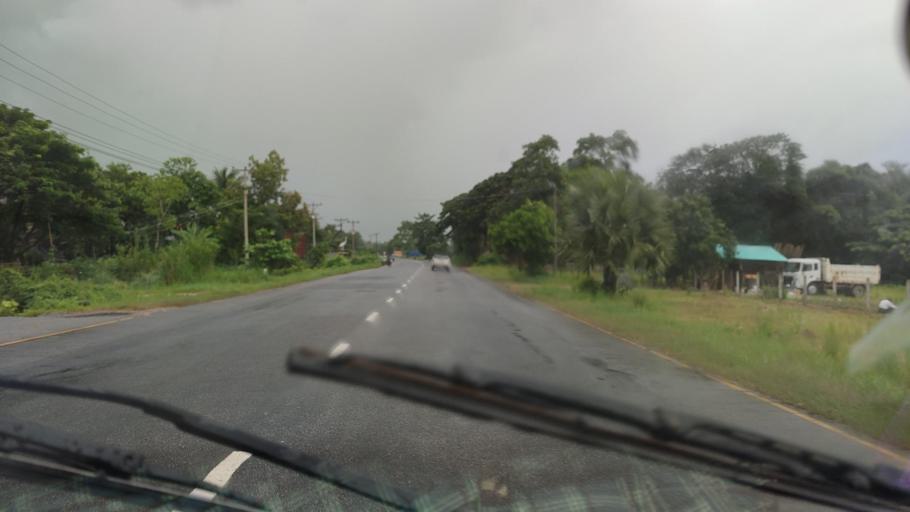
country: MM
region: Bago
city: Bago
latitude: 17.5937
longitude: 96.5649
